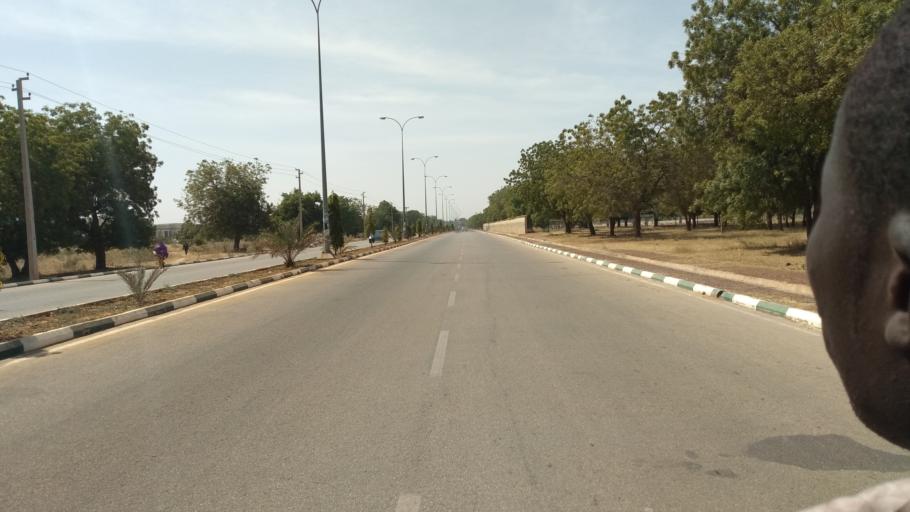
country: NG
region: Jigawa
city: Dutse
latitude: 11.6848
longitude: 9.3382
